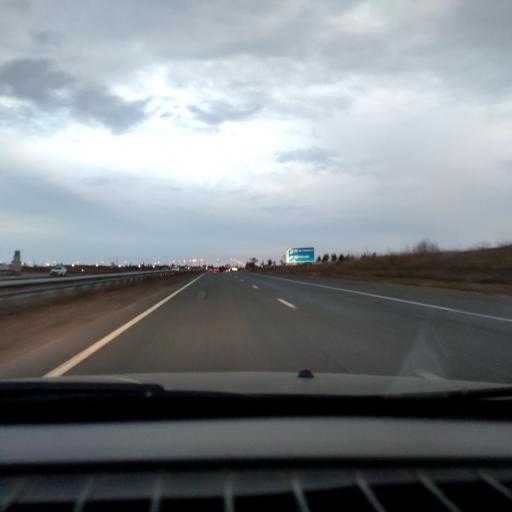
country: RU
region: Samara
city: Zhigulevsk
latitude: 53.5076
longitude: 49.5382
